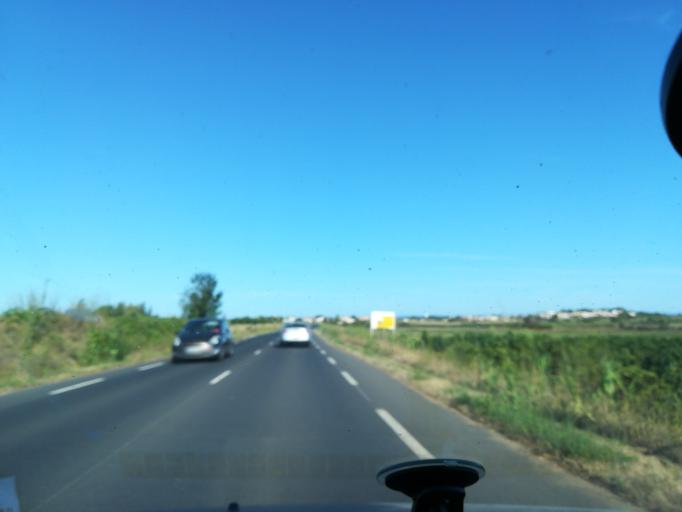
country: FR
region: Languedoc-Roussillon
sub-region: Departement de l'Herault
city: Portiragnes
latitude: 43.2948
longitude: 3.3558
